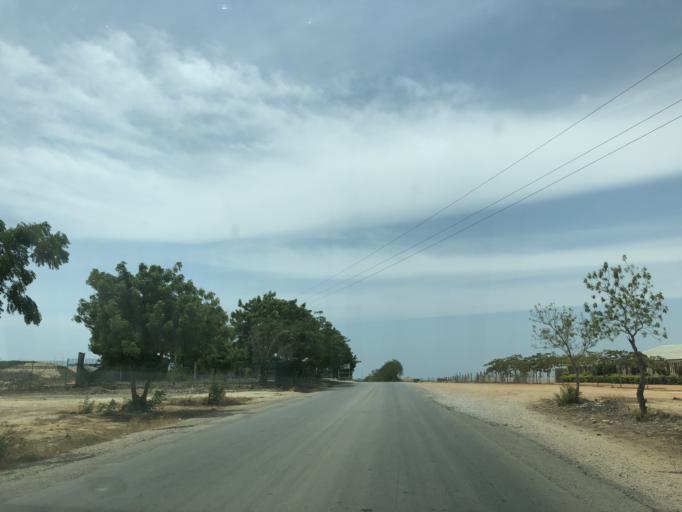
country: AO
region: Cuanza Sul
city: Sumbe
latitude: -10.7512
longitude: 13.7904
